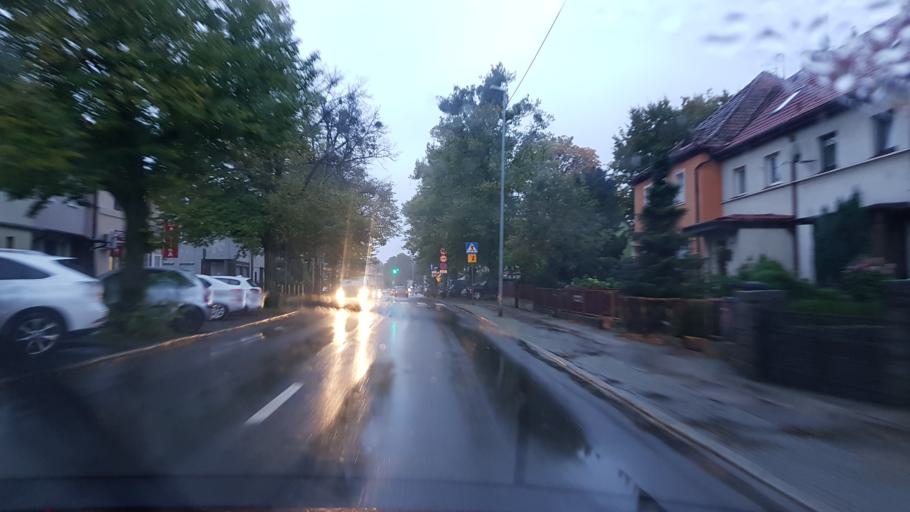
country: PL
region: West Pomeranian Voivodeship
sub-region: Szczecin
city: Szczecin
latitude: 53.4422
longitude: 14.5144
